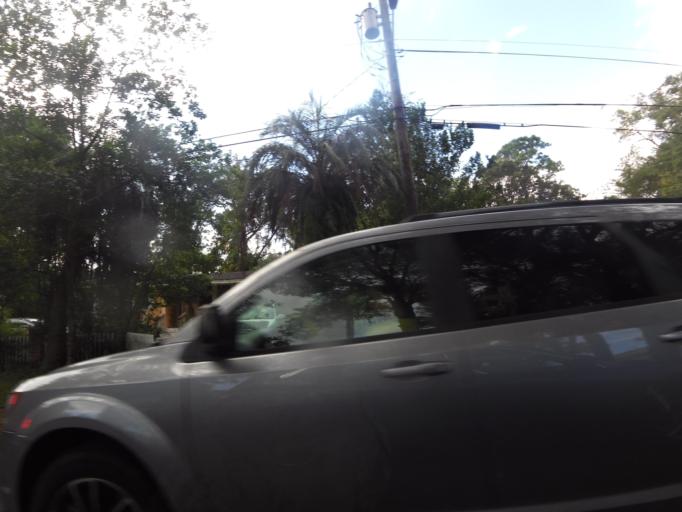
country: US
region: Florida
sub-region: Duval County
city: Jacksonville
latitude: 30.3255
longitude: -81.5887
